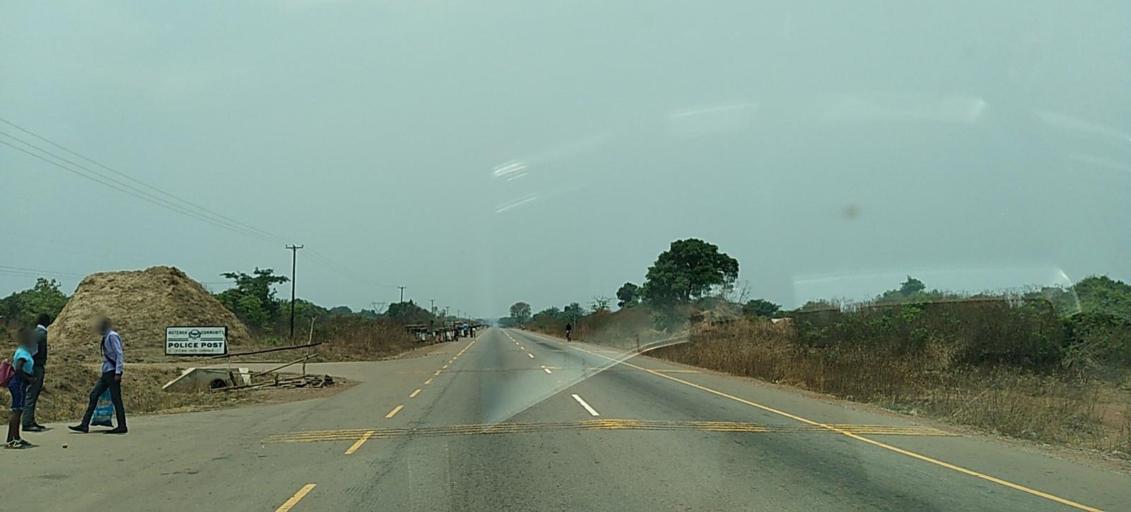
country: ZM
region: Copperbelt
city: Chililabombwe
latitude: -12.3933
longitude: 27.3628
